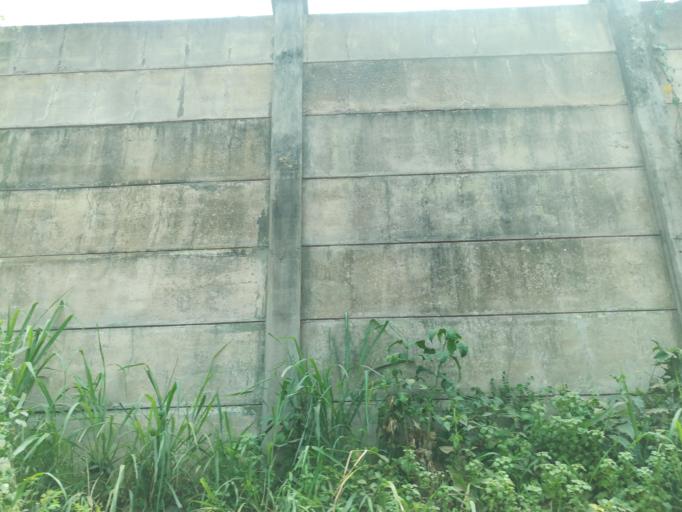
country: NG
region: Lagos
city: Ebute Ikorodu
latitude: 6.5763
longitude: 3.4893
